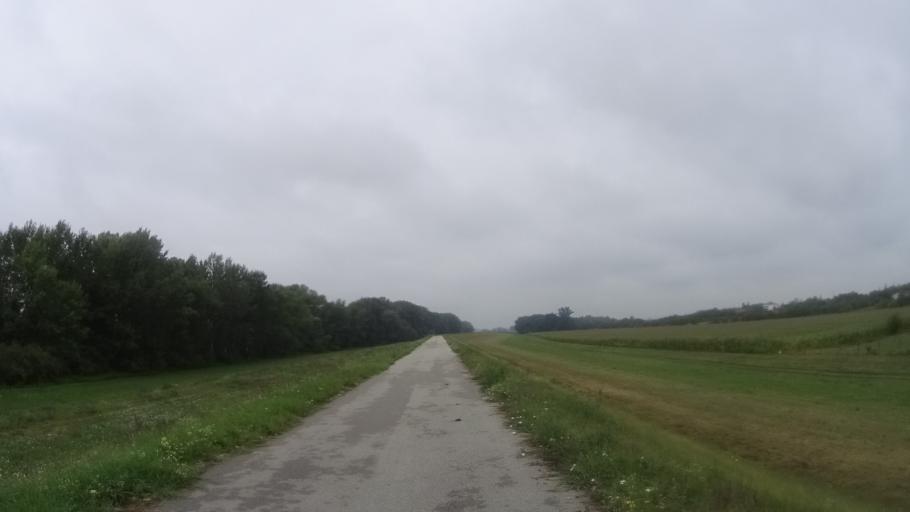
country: HU
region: Komarom-Esztergom
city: Almasfuzito
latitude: 47.7452
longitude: 18.2307
